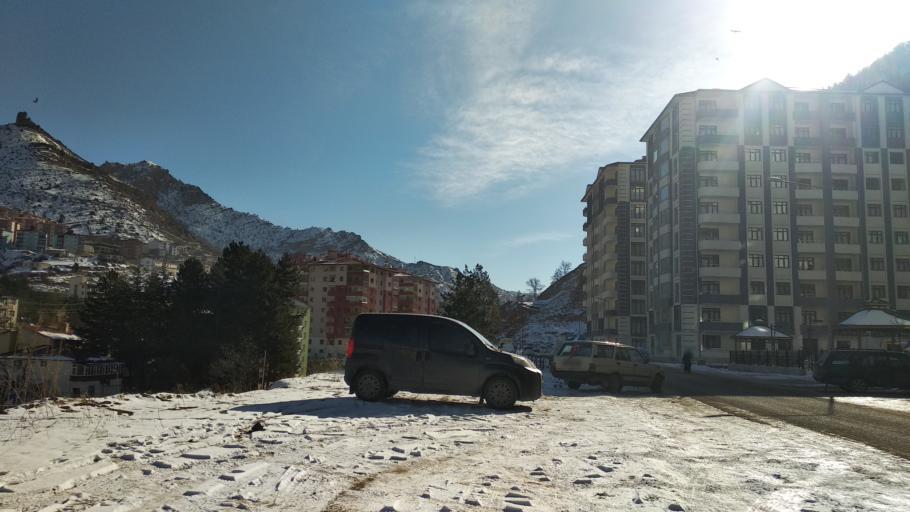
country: TR
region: Gumushane
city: Gumushkhane
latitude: 40.4513
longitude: 39.4927
